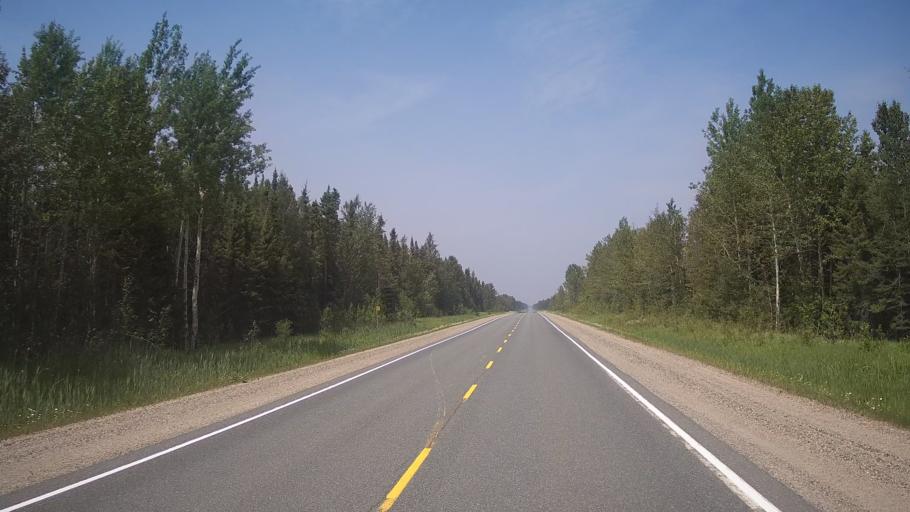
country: CA
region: Ontario
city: Timmins
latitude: 48.8247
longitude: -81.3711
